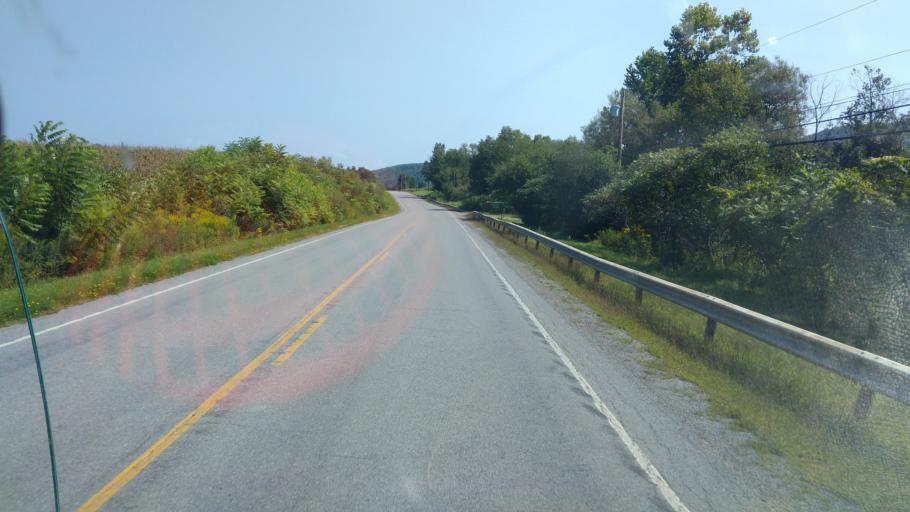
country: US
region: New York
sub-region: Allegany County
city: Friendship
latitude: 42.2219
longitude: -78.0973
